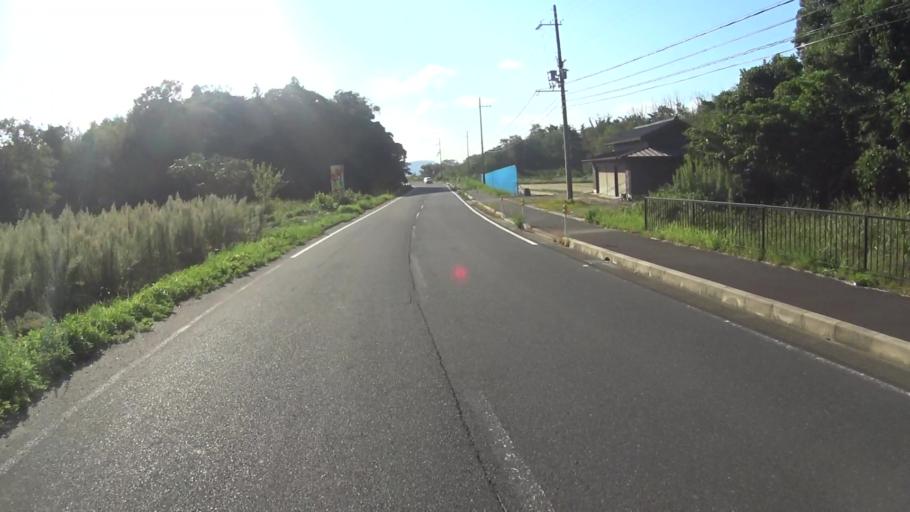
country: JP
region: Hyogo
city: Toyooka
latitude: 35.6445
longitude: 134.9475
